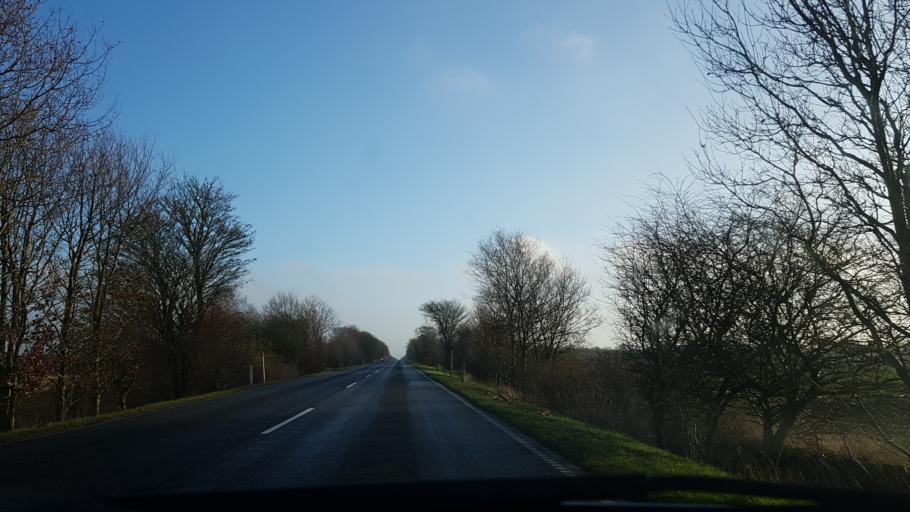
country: DK
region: South Denmark
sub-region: Haderslev Kommune
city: Vojens
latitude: 55.1866
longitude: 9.2221
